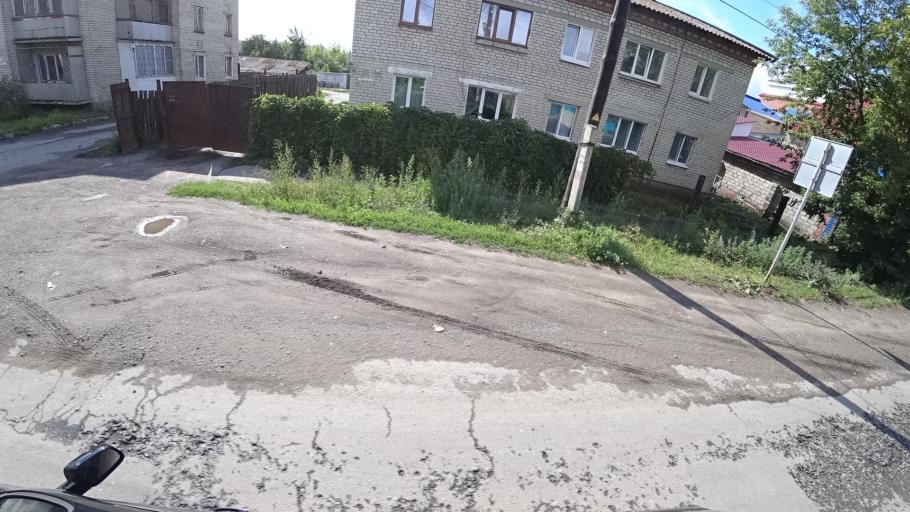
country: RU
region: Sverdlovsk
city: Kamyshlov
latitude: 56.8482
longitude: 62.6920
